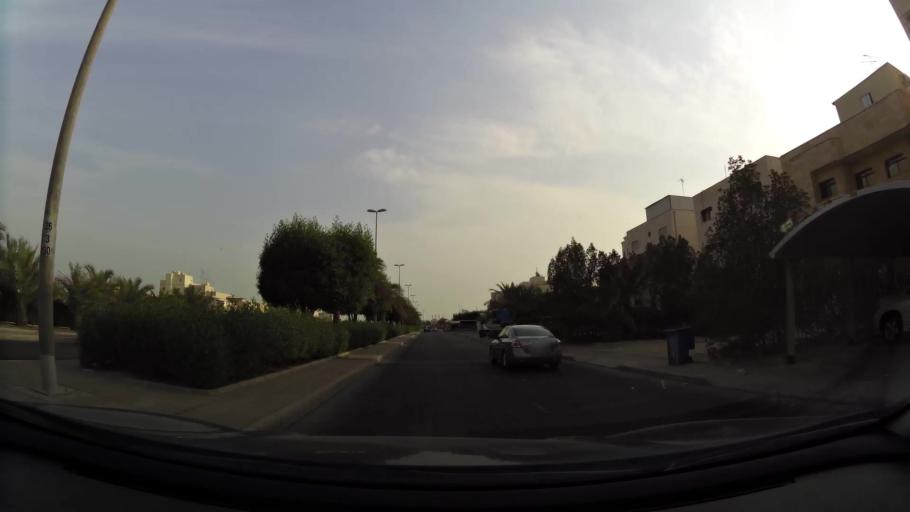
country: KW
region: Mubarak al Kabir
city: Mubarak al Kabir
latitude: 29.1875
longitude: 48.0714
